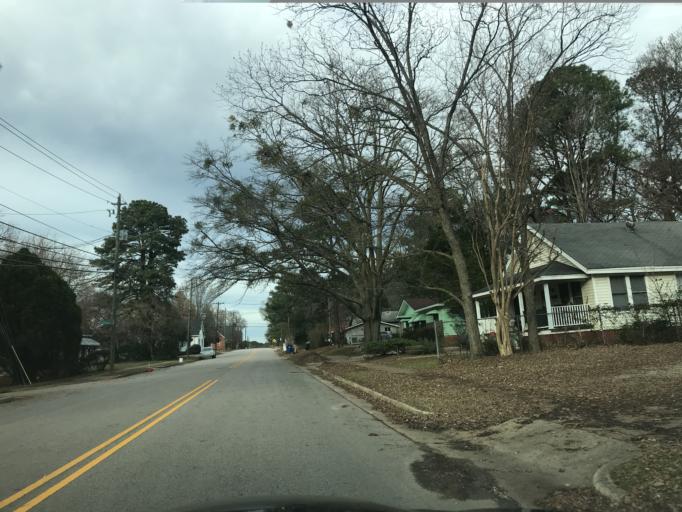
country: US
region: North Carolina
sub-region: Wake County
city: West Raleigh
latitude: 35.7906
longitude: -78.6937
